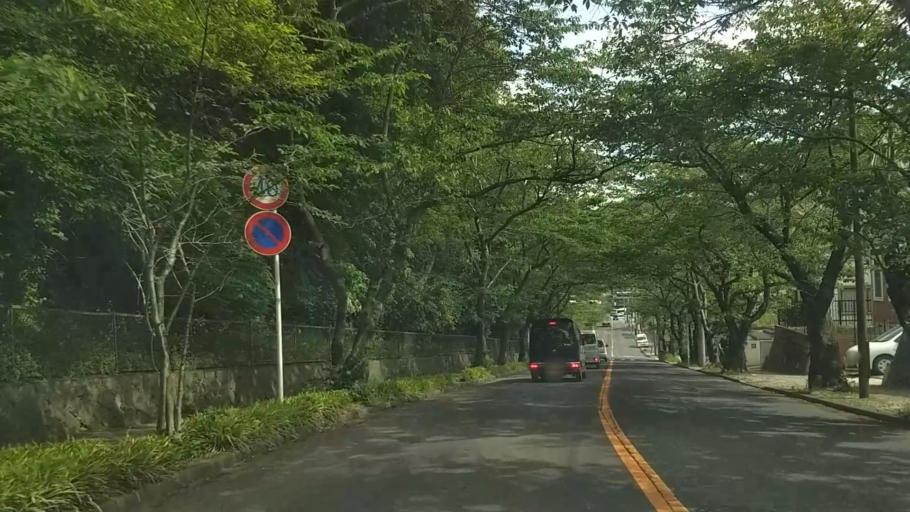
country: JP
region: Kanagawa
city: Zushi
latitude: 35.3169
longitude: 139.5767
